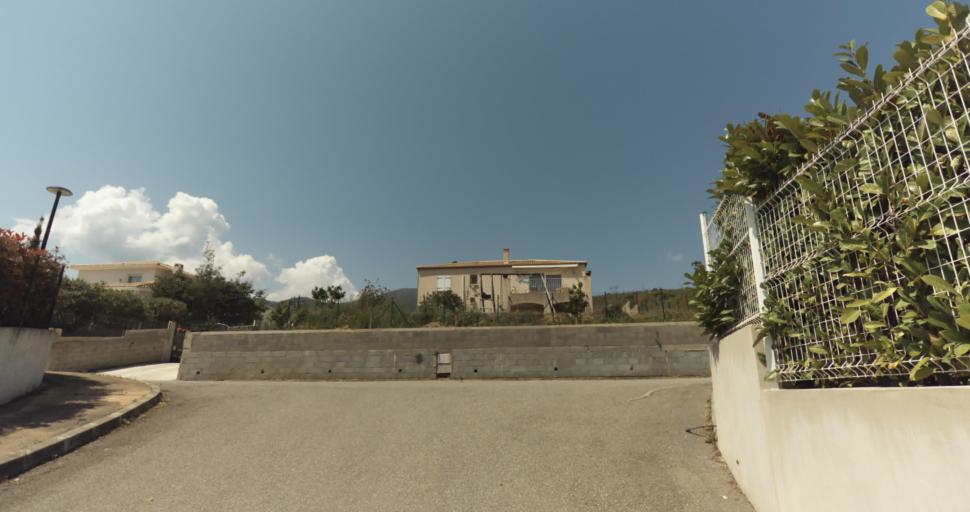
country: FR
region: Corsica
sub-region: Departement de la Haute-Corse
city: Biguglia
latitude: 42.6006
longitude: 9.4308
